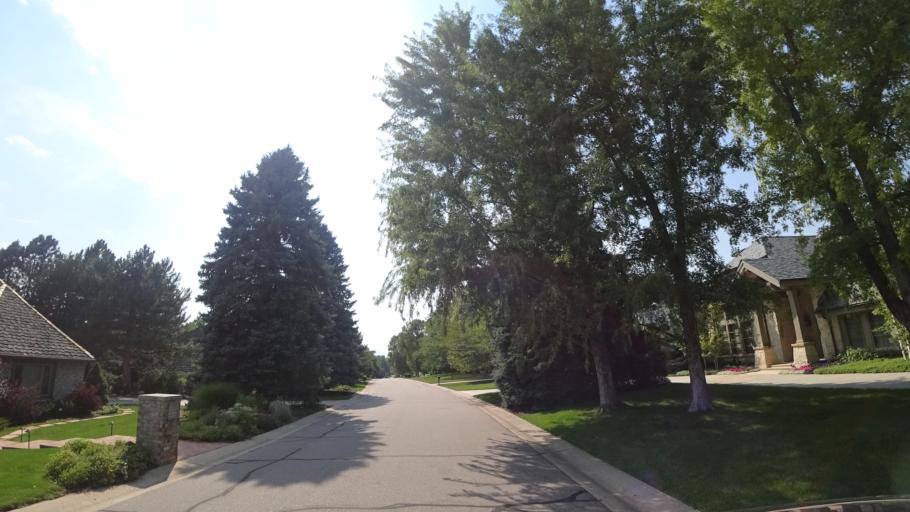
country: US
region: Colorado
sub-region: Arapahoe County
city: Greenwood Village
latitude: 39.6128
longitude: -104.9655
